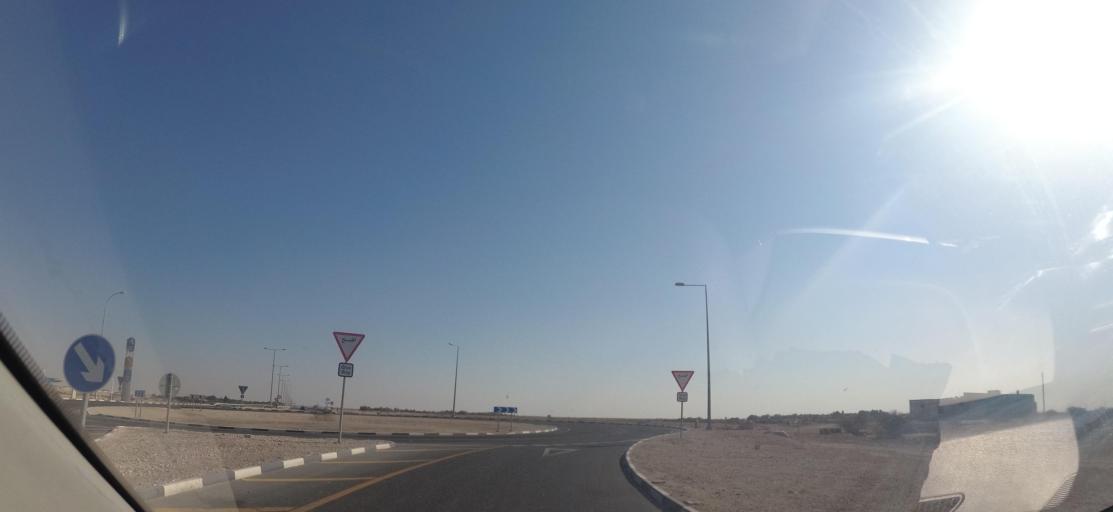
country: QA
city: Al Jumayliyah
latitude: 25.6175
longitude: 51.0842
